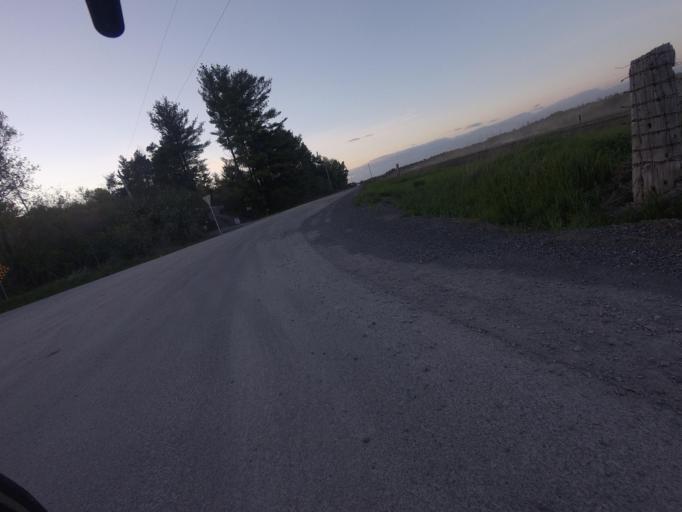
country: CA
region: Ontario
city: Arnprior
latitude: 45.4004
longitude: -76.1998
